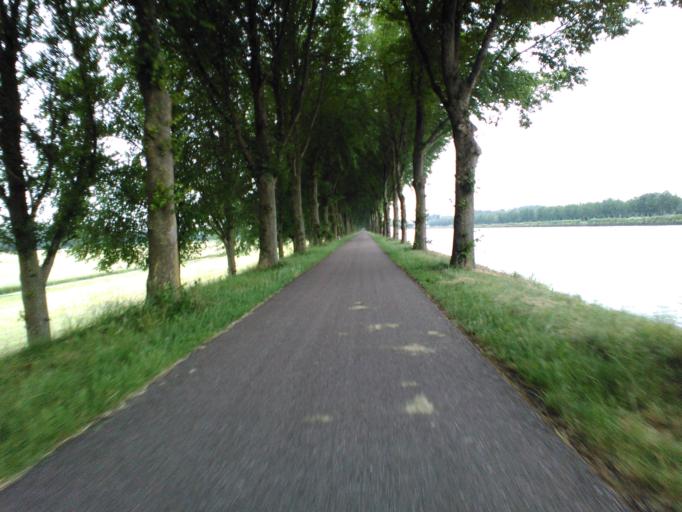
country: NL
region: North Holland
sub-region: Gemeente Amsterdam
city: Driemond
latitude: 52.2953
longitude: 5.0208
